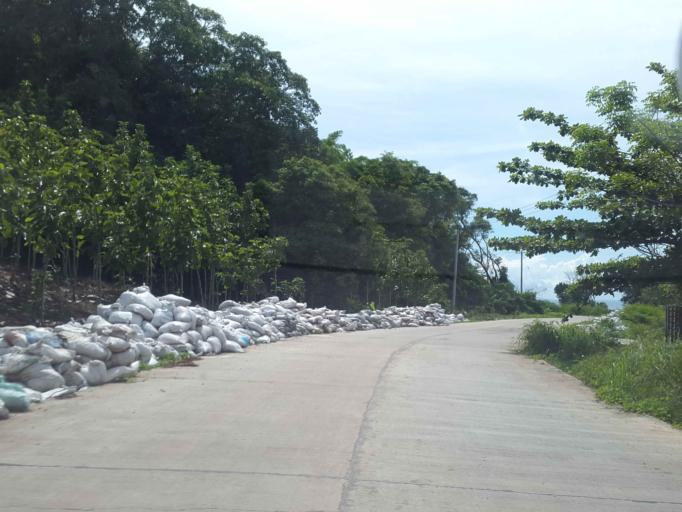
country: ID
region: Banten
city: Citeureup
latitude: -6.5047
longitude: 105.6417
